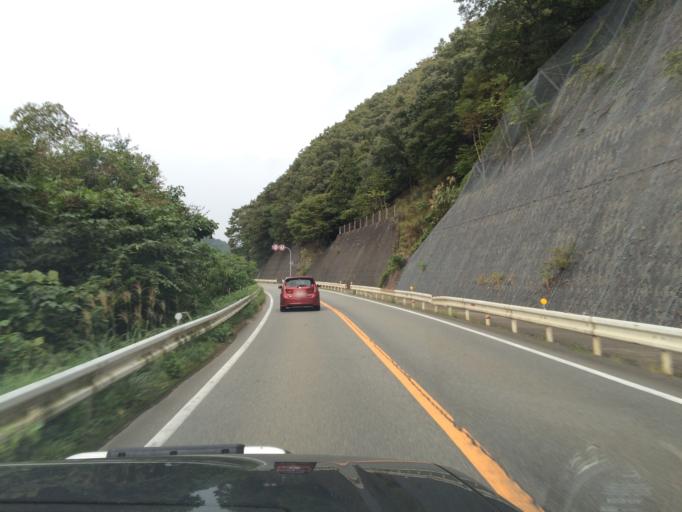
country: JP
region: Hyogo
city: Toyooka
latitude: 35.3621
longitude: 134.8275
